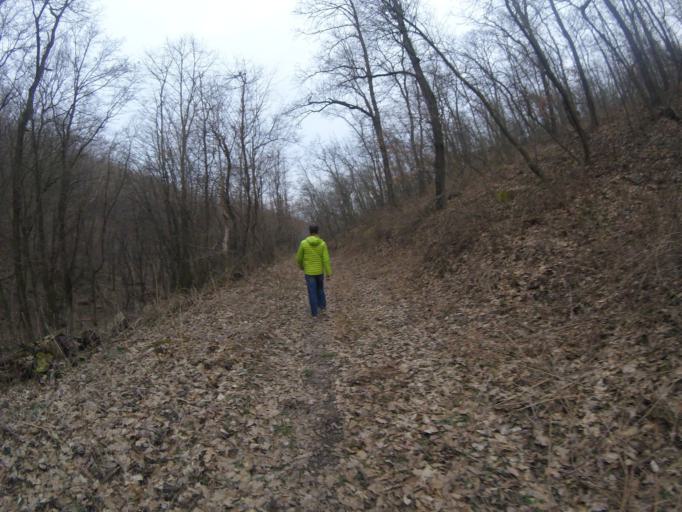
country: HU
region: Baranya
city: Mecseknadasd
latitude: 46.1410
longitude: 18.5184
